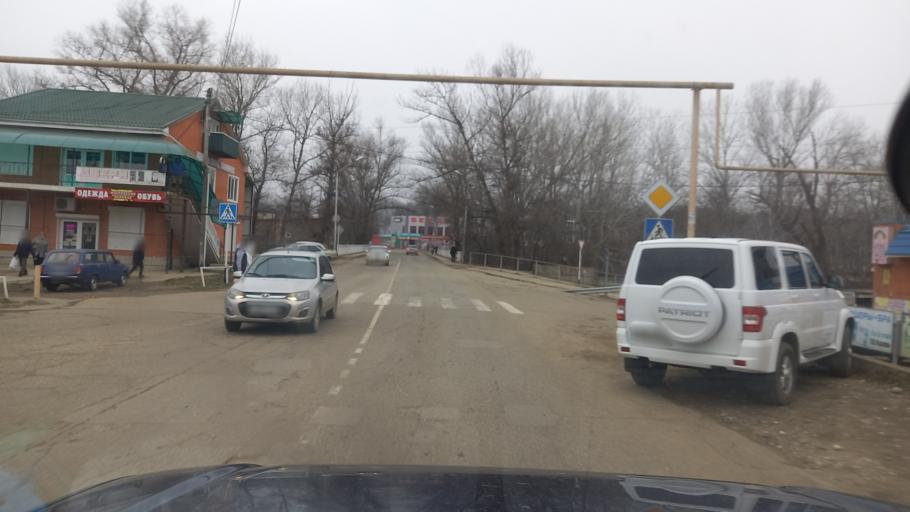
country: RU
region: Krasnodarskiy
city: Apsheronsk
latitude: 44.4622
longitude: 39.7384
